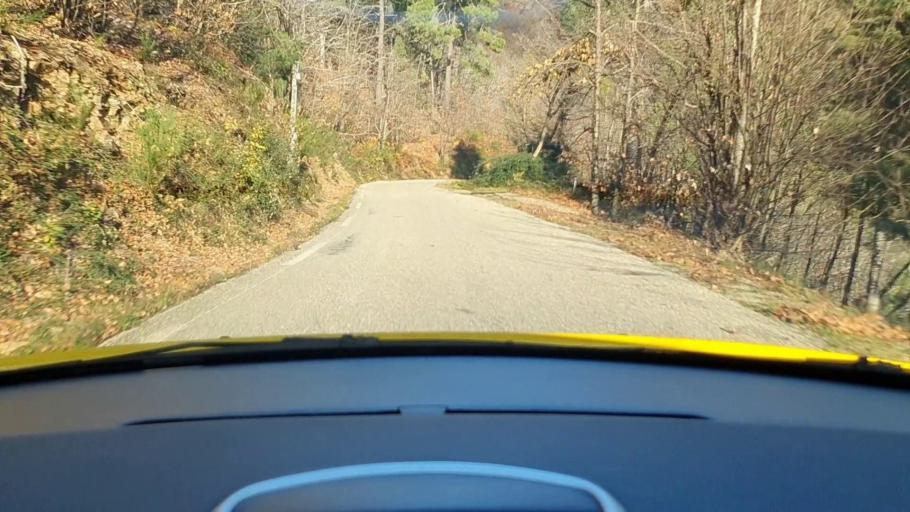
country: FR
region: Languedoc-Roussillon
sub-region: Departement du Gard
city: Branoux-les-Taillades
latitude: 44.2782
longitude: 3.9729
